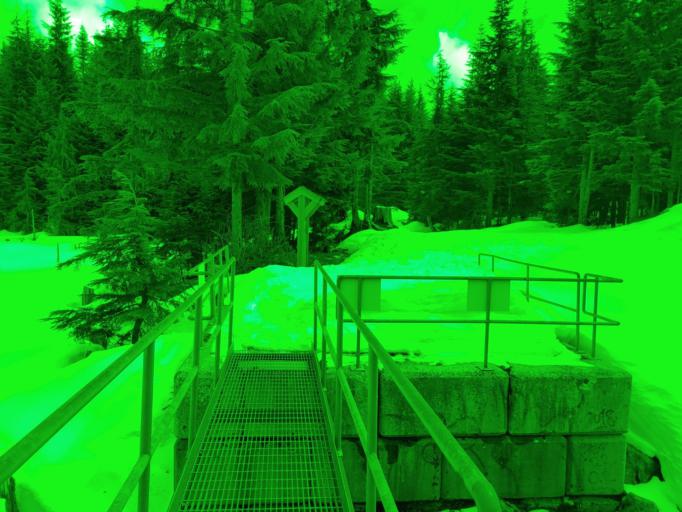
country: CA
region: British Columbia
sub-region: Greater Vancouver Regional District
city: Anmore
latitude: 49.3360
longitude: -122.8163
